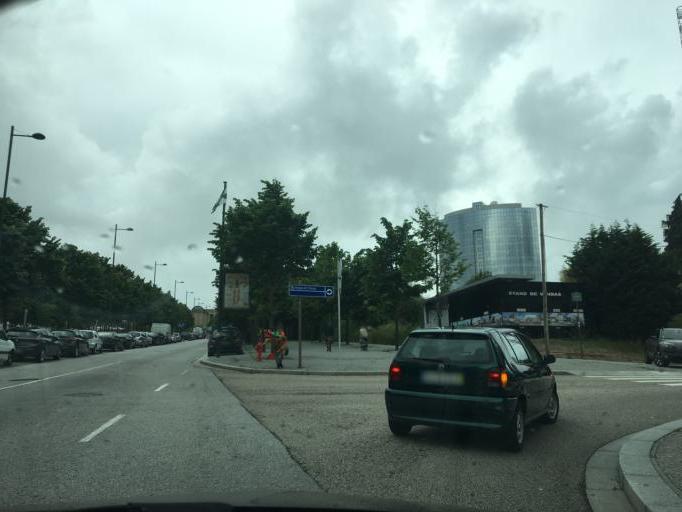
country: PT
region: Porto
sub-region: Porto
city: Porto
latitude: 41.1632
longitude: -8.5860
